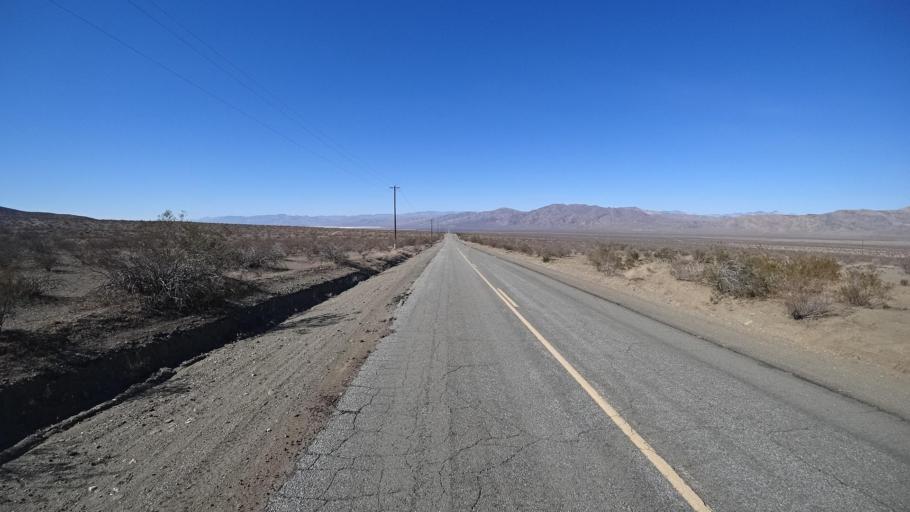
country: US
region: California
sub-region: Kern County
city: Ridgecrest
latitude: 35.3807
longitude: -117.6800
